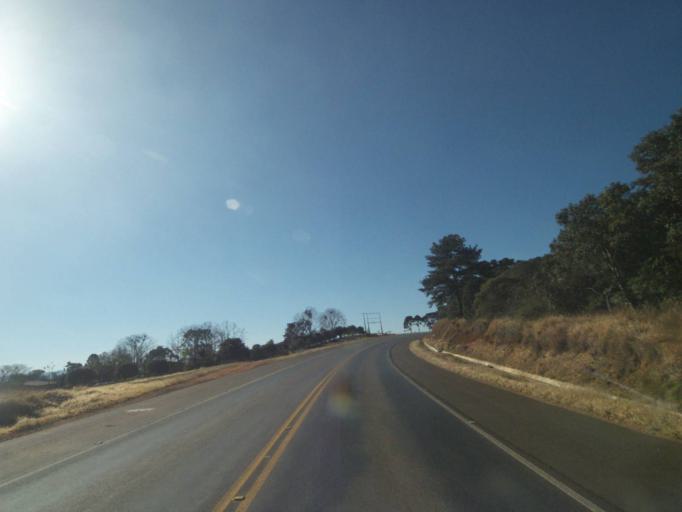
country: BR
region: Parana
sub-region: Tibagi
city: Tibagi
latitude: -24.6974
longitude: -50.4458
